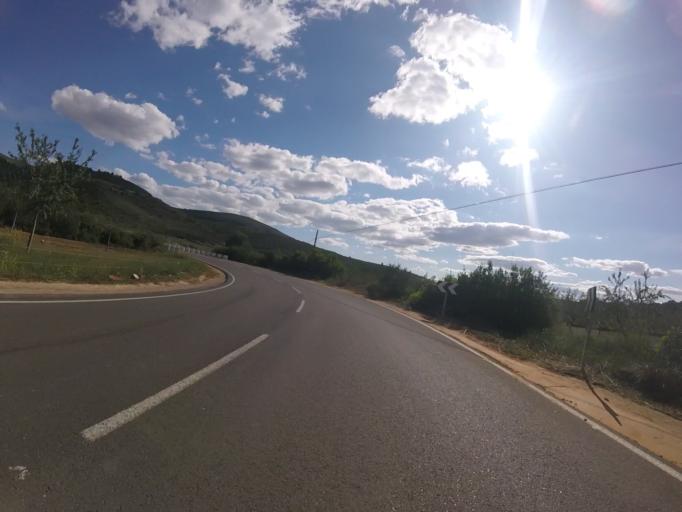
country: ES
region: Valencia
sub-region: Provincia de Castello
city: Cuevas de Vinroma
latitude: 40.3009
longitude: 0.1652
